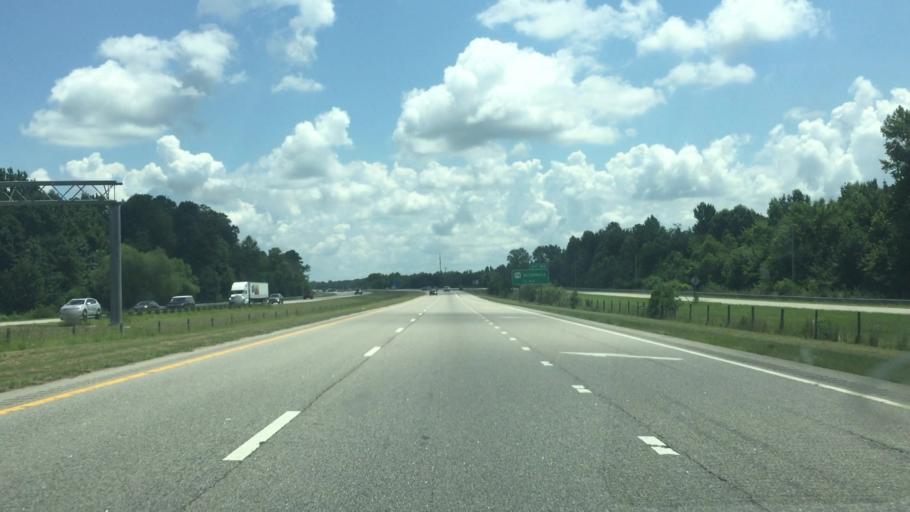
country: US
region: North Carolina
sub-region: Robeson County
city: Fairmont
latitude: 34.5919
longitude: -79.1036
